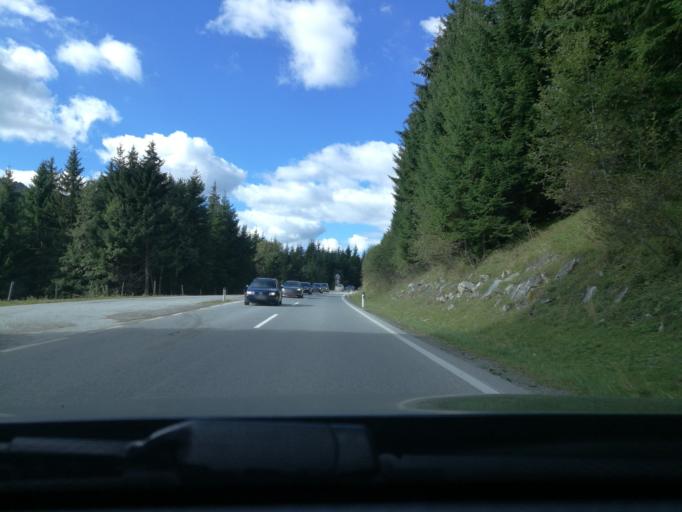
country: AT
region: Salzburg
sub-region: Politischer Bezirk Zell am See
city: Krimml
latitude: 47.2435
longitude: 12.0968
